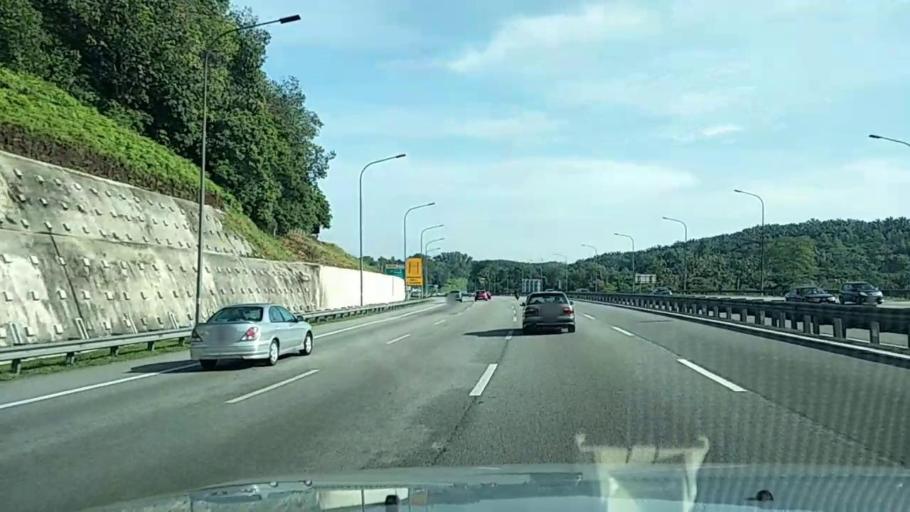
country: MY
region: Negeri Sembilan
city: Kampung Baharu Nilai
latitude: 2.8388
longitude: 101.7902
